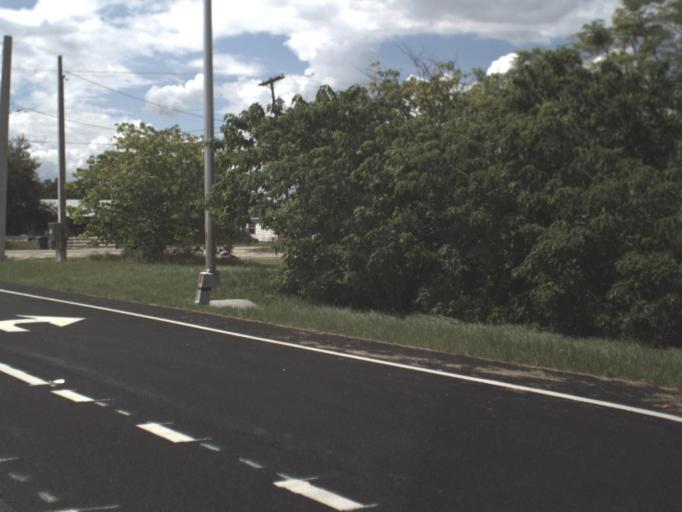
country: US
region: Florida
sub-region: Polk County
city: Wahneta
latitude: 27.9164
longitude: -81.7175
